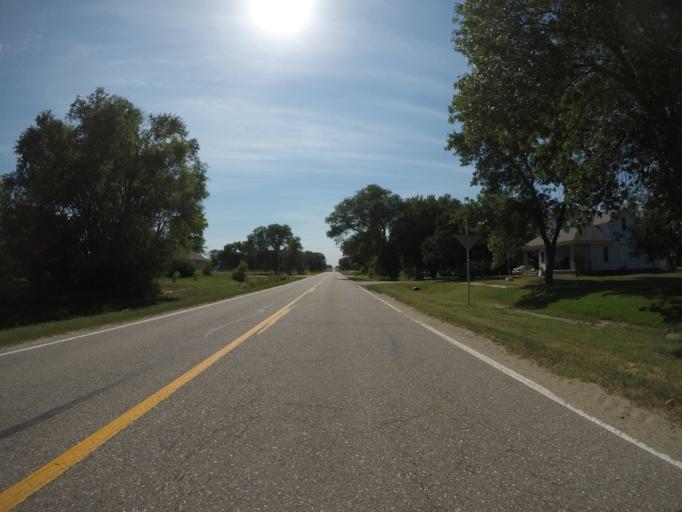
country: US
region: Nebraska
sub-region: Adams County
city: Hastings
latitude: 40.4374
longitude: -98.4413
